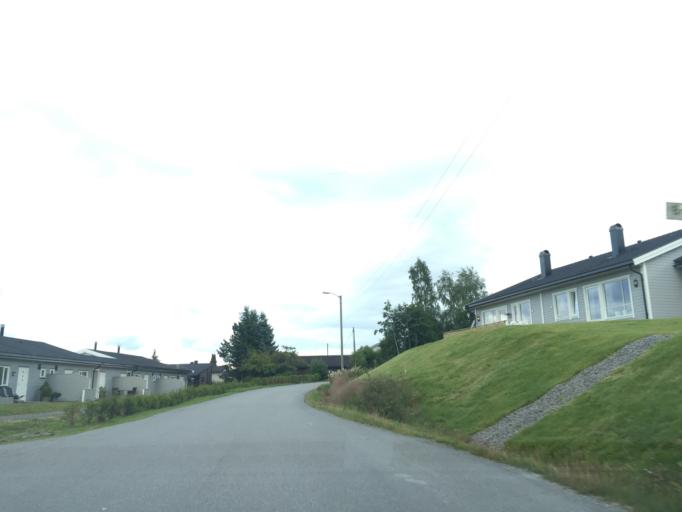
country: NO
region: Hedmark
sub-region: Kongsvinger
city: Kongsvinger
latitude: 60.1832
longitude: 11.9846
